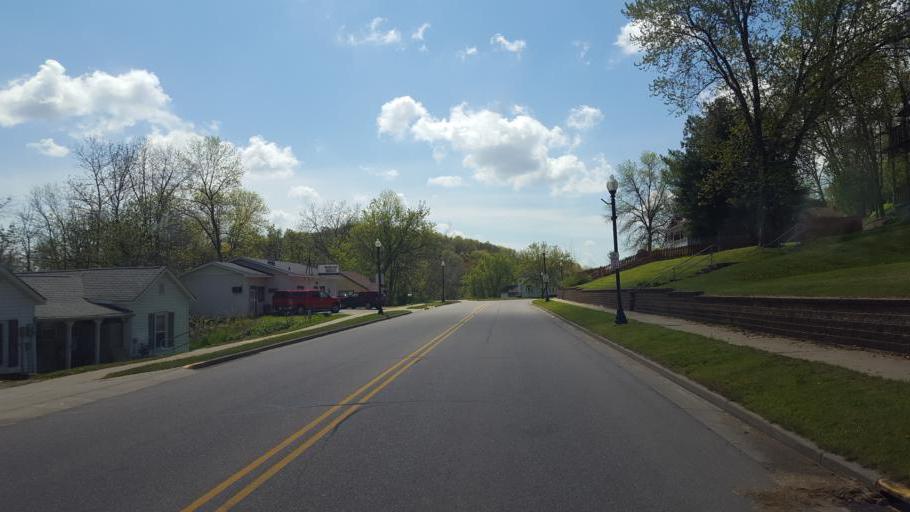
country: US
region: Wisconsin
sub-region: Juneau County
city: Elroy
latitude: 43.7365
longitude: -90.2686
